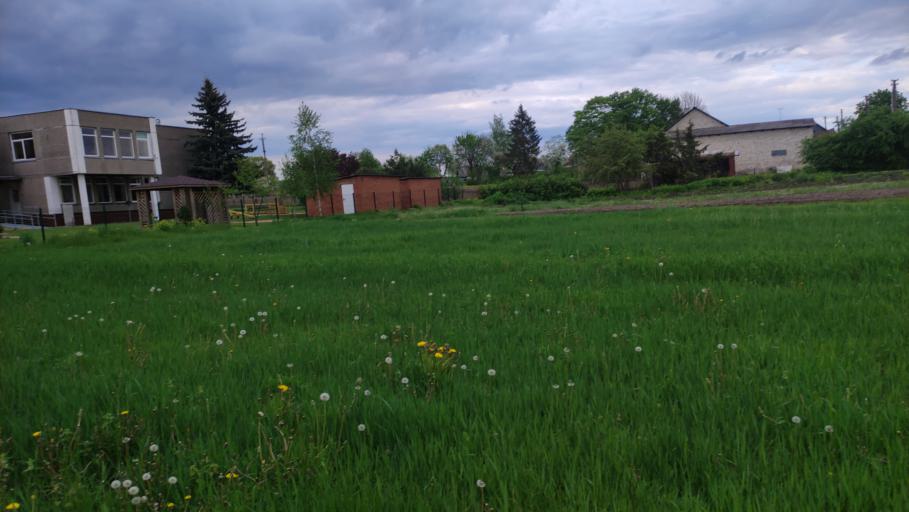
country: LT
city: Jieznas
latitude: 54.5023
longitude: 24.2507
